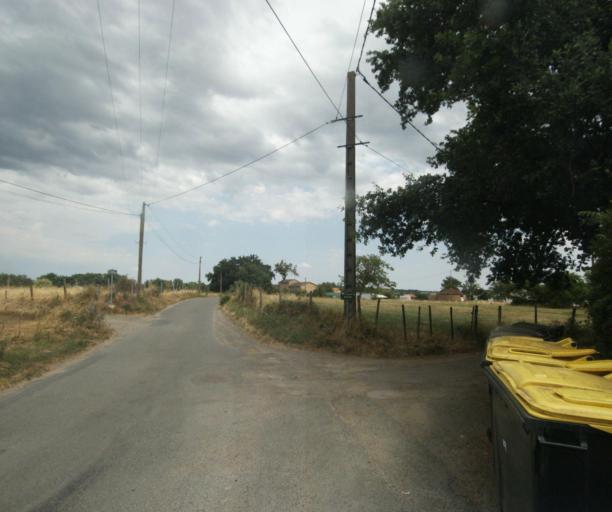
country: FR
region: Rhone-Alpes
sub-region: Departement du Rhone
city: Saint-Romain-de-Popey
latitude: 45.8830
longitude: 4.5300
